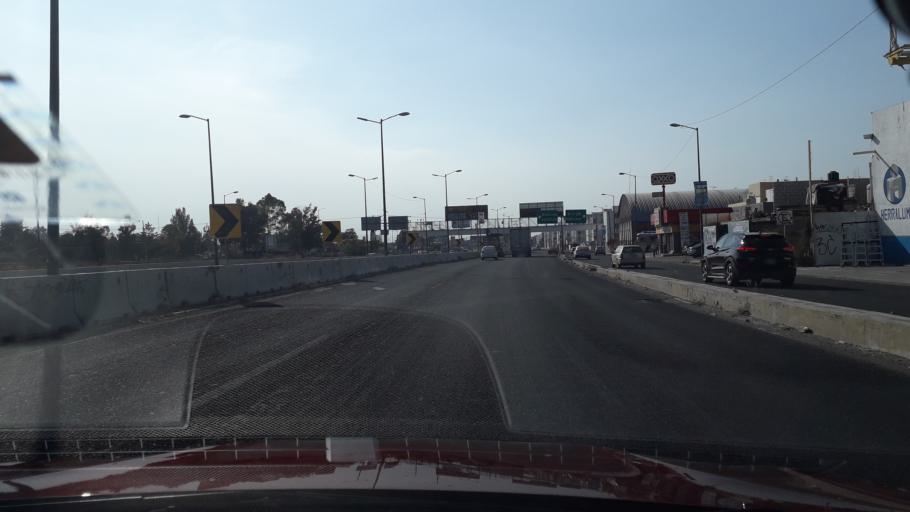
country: MX
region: Puebla
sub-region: Puebla
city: El Capulo (La Quebradora)
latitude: 18.9855
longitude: -98.2332
